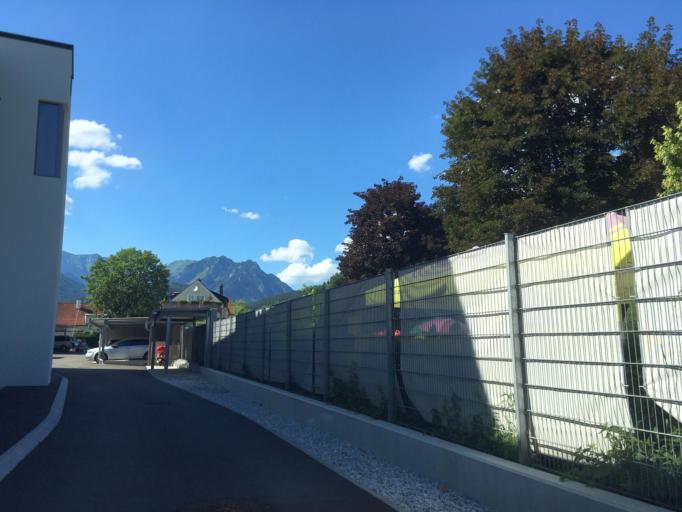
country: AT
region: Styria
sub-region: Politischer Bezirk Leoben
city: Trofaiach
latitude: 47.4234
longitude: 15.0119
